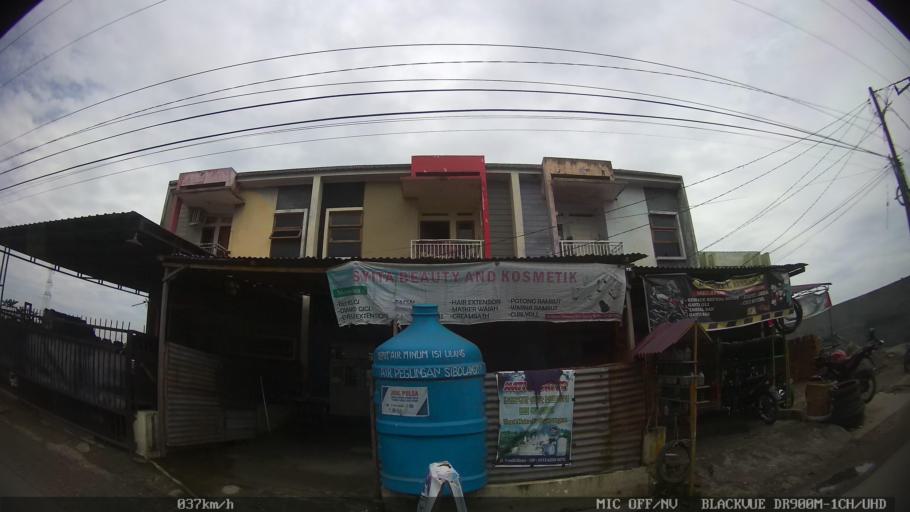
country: ID
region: North Sumatra
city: Sunggal
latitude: 3.6145
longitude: 98.5913
